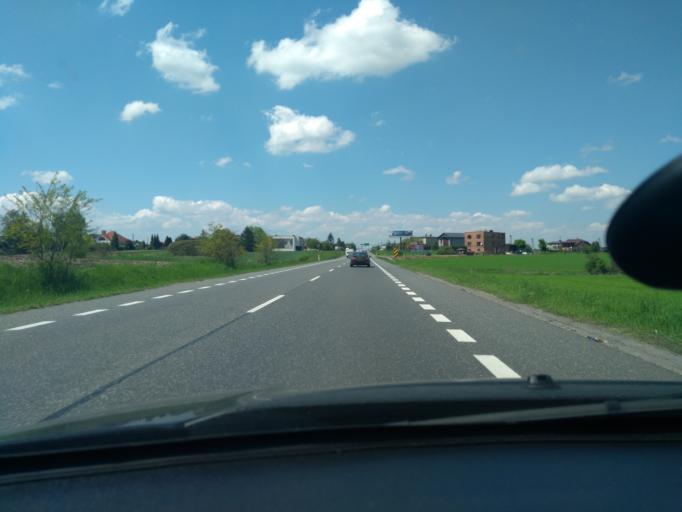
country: PL
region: Silesian Voivodeship
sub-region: Powiat gliwicki
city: Paniowki
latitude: 50.2309
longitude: 18.7962
